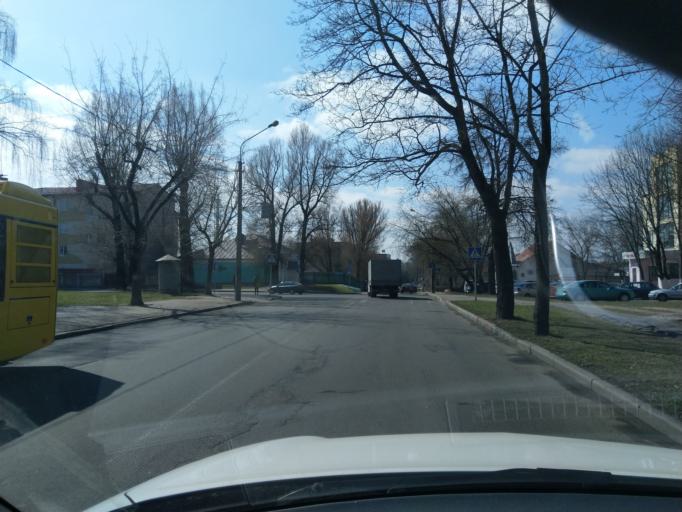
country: BY
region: Minsk
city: Syenitsa
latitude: 53.8727
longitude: 27.5108
